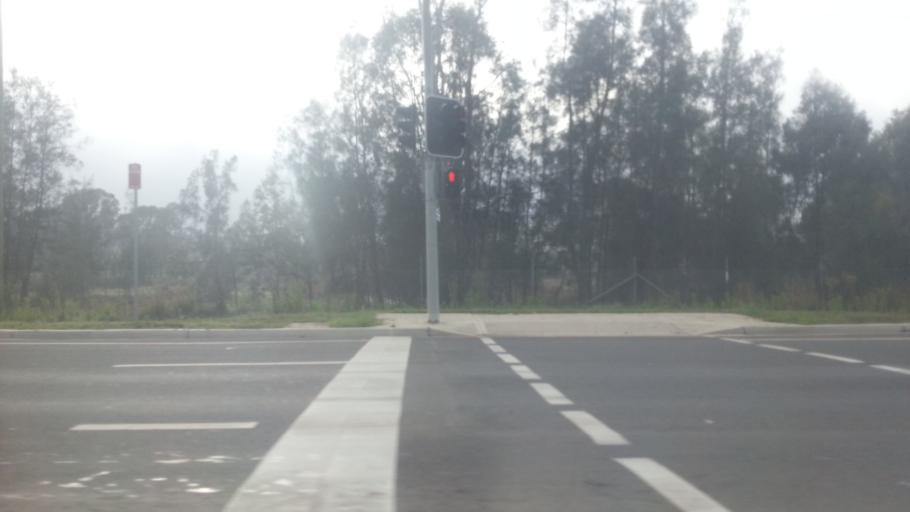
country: AU
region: New South Wales
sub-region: Penrith Municipality
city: Glenmore Park
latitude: -33.8052
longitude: 150.6961
